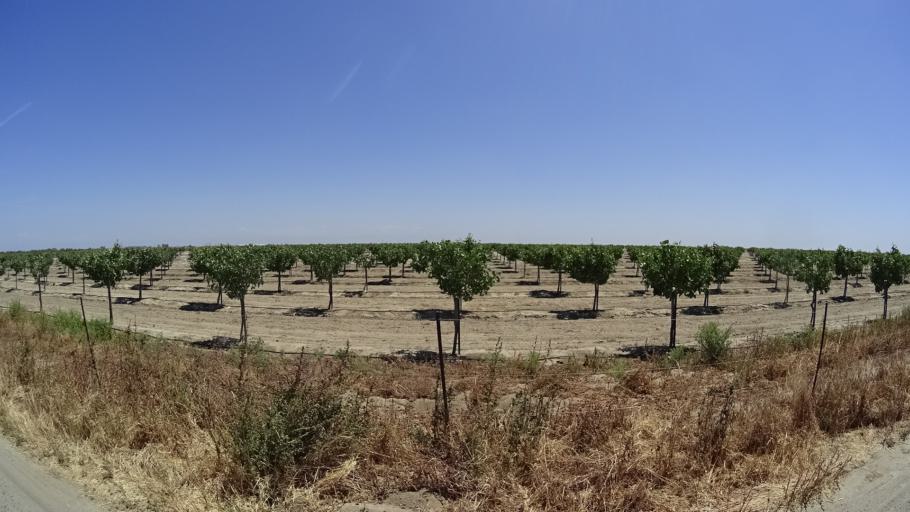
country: US
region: California
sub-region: Kings County
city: Stratford
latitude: 36.2095
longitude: -119.7445
